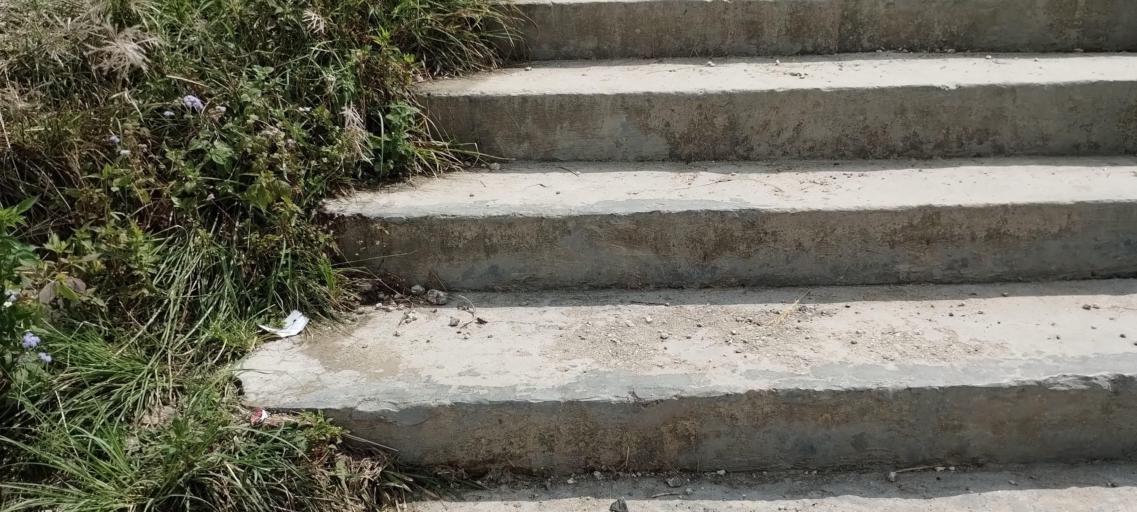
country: NP
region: Central Region
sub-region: Bagmati Zone
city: Kathmandu
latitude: 27.7897
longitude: 85.3608
